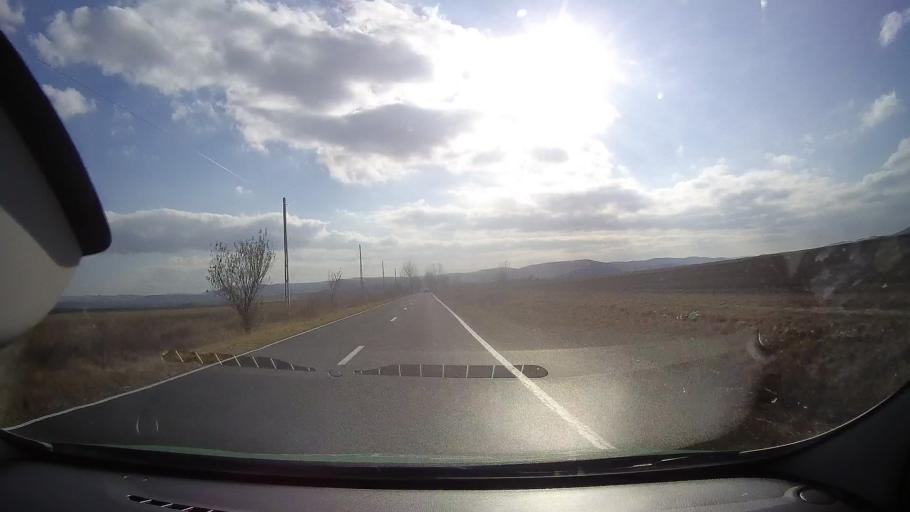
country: RO
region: Tulcea
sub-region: Comuna Nalbant
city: Nicolae Balcescu
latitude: 45.0087
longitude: 28.5983
